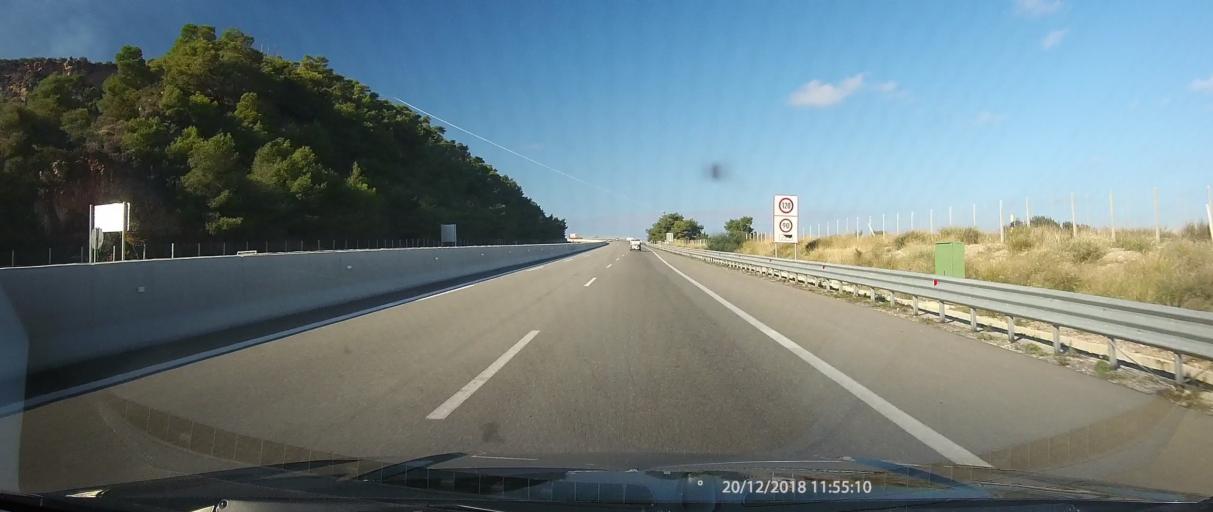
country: GR
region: West Greece
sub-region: Nomos Achaias
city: Siliveniotika
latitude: 38.1683
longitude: 22.3270
